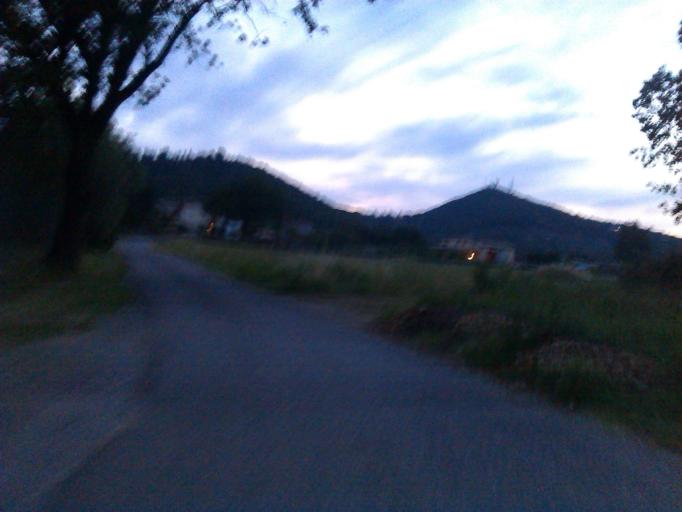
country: IT
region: Tuscany
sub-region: Province of Arezzo
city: Battifolle-Ruscello-Poggiola
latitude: 43.4470
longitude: 11.7931
